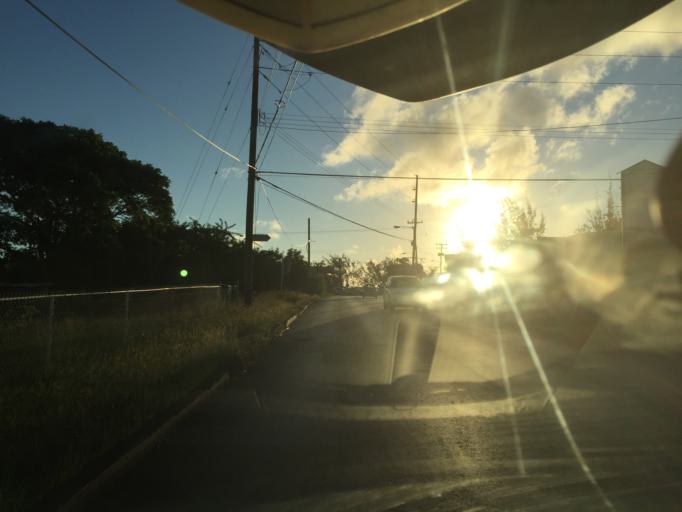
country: BB
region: Christ Church
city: Oistins
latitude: 13.0779
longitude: -59.5140
